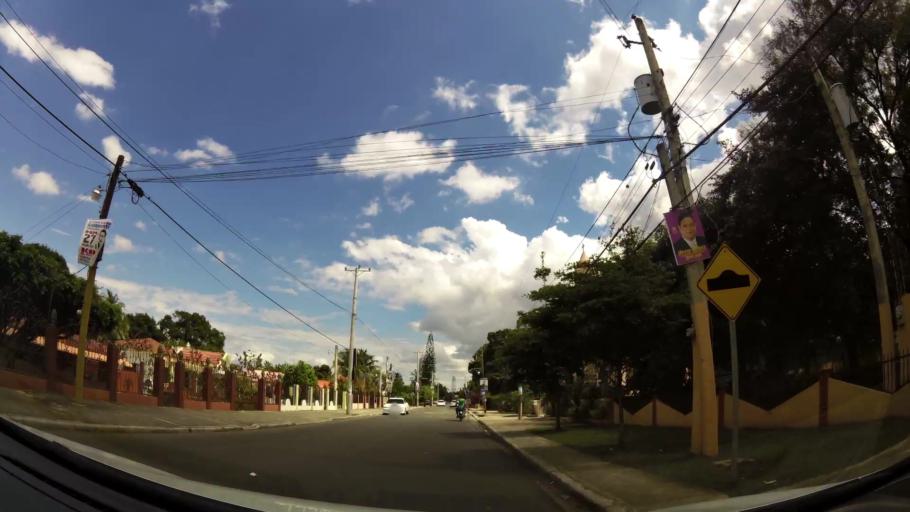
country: DO
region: Santiago
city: Licey al Medio
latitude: 19.3907
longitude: -70.6393
